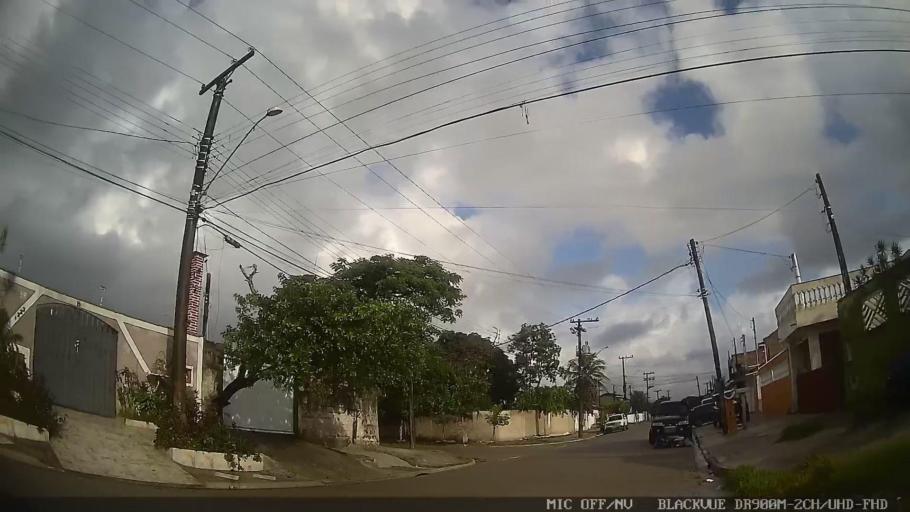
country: BR
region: Sao Paulo
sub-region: Itanhaem
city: Itanhaem
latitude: -24.1840
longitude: -46.8573
